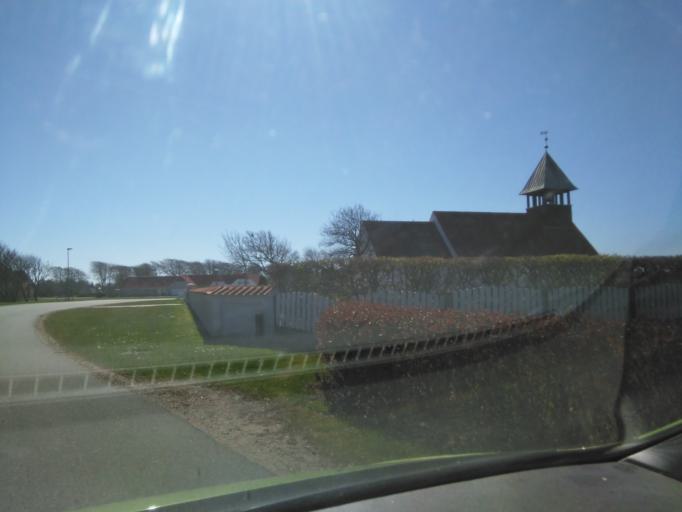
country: DK
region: South Denmark
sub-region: Varde Kommune
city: Oksbol
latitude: 55.5544
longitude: 8.2297
